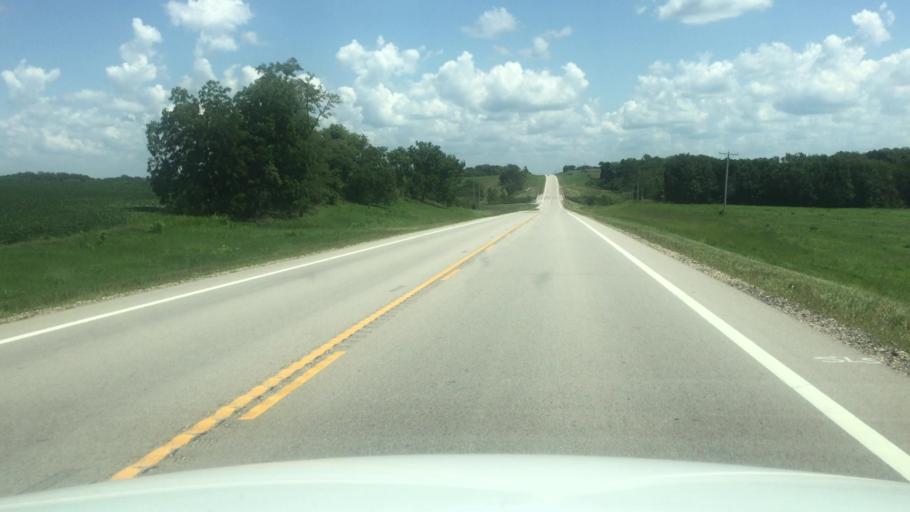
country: US
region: Kansas
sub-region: Brown County
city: Horton
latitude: 39.6672
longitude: -95.4783
